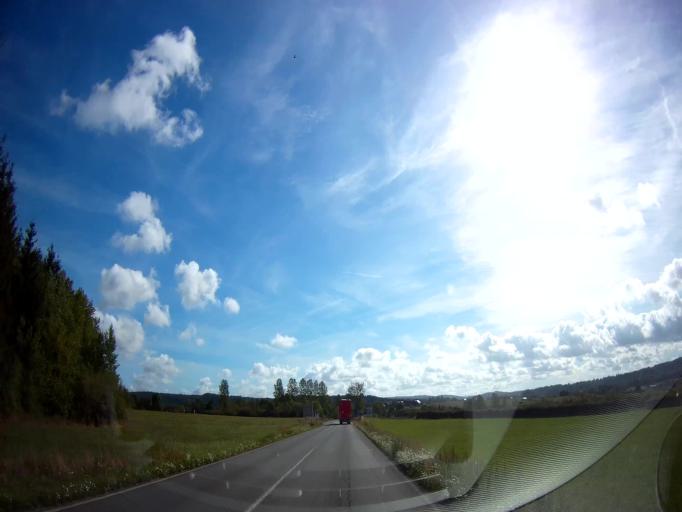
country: BE
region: Wallonia
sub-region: Province de Namur
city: Rochefort
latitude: 50.1672
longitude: 5.1926
